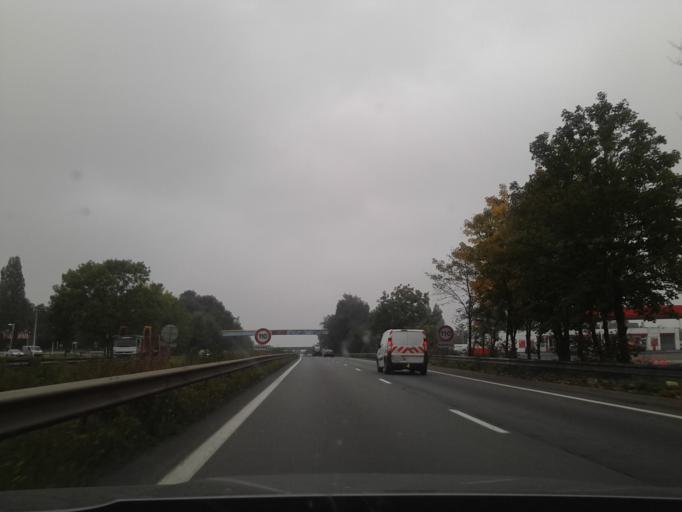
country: FR
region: Nord-Pas-de-Calais
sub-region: Departement du Nord
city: La Sentinelle
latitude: 50.3405
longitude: 3.4698
